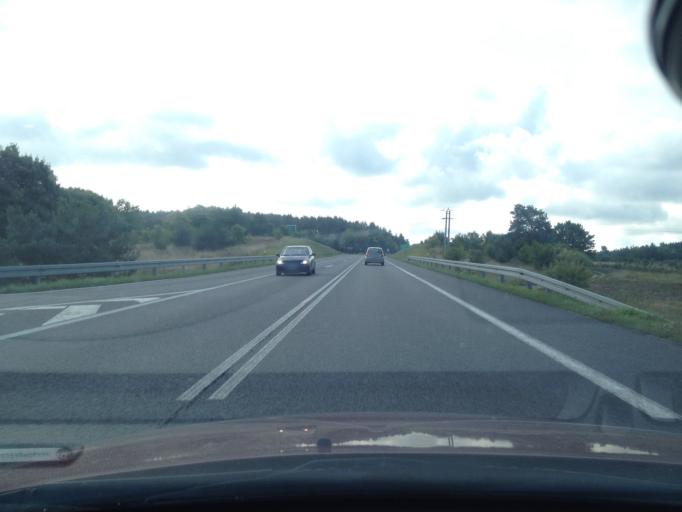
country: PL
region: West Pomeranian Voivodeship
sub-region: Powiat goleniowski
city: Przybiernow
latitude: 53.7480
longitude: 14.7742
